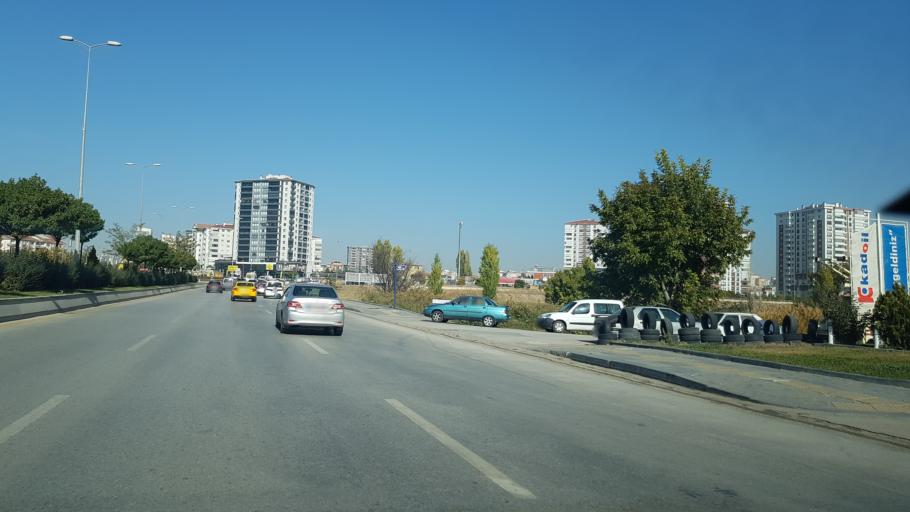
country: TR
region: Ankara
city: Etimesgut
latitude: 39.9684
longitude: 32.6081
